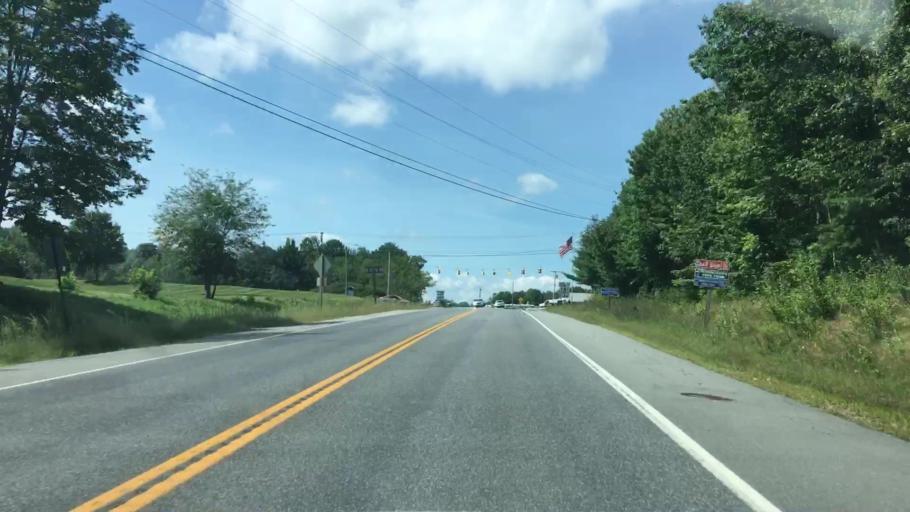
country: US
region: Maine
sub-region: Kennebec County
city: Monmouth
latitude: 44.2684
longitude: -70.0280
